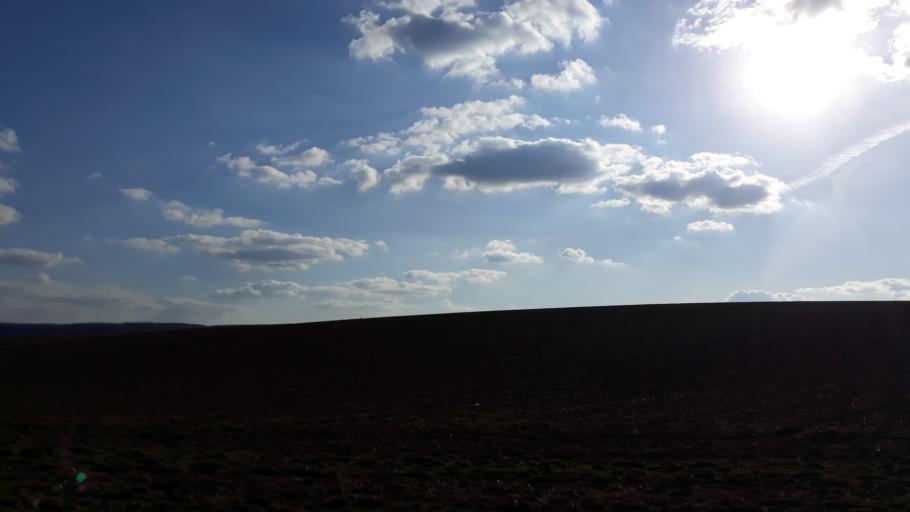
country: FR
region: Picardie
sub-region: Departement de l'Oise
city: Bornel
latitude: 49.2077
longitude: 2.2184
